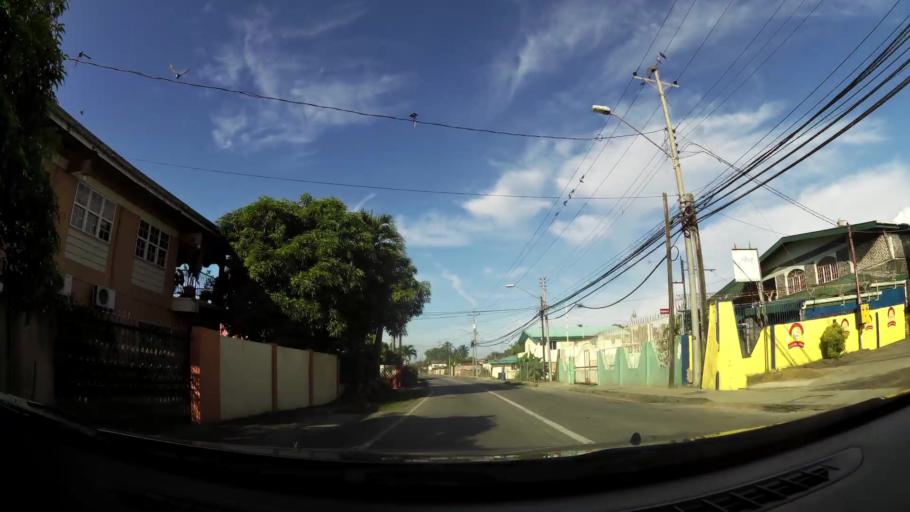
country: TT
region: Chaguanas
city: Chaguanas
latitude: 10.5472
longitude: -61.3501
